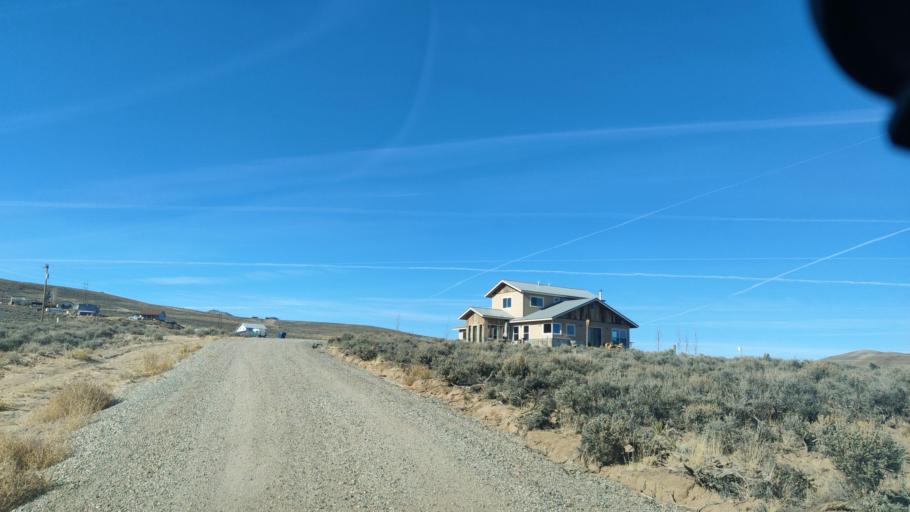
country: US
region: Colorado
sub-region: Gunnison County
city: Gunnison
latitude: 38.5432
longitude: -106.9509
